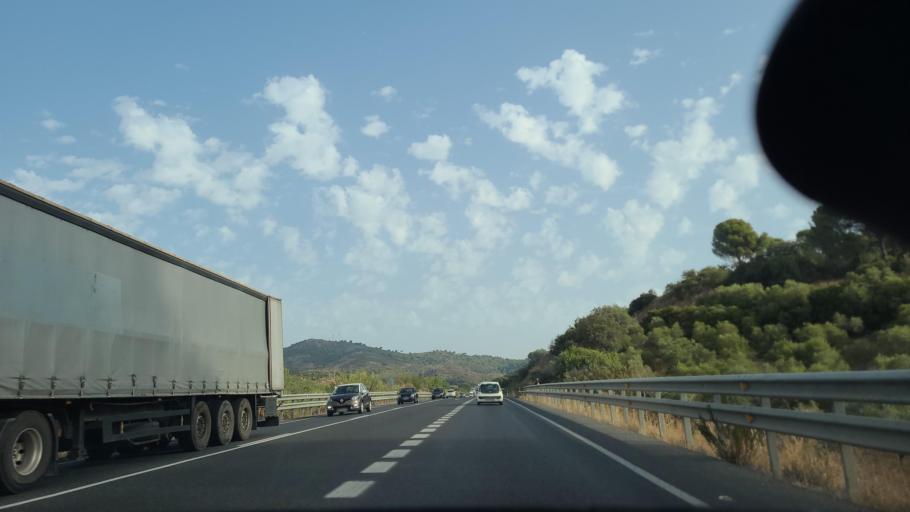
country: ES
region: Andalusia
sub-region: Province of Cordoba
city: Cordoba
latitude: 37.9631
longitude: -4.7673
